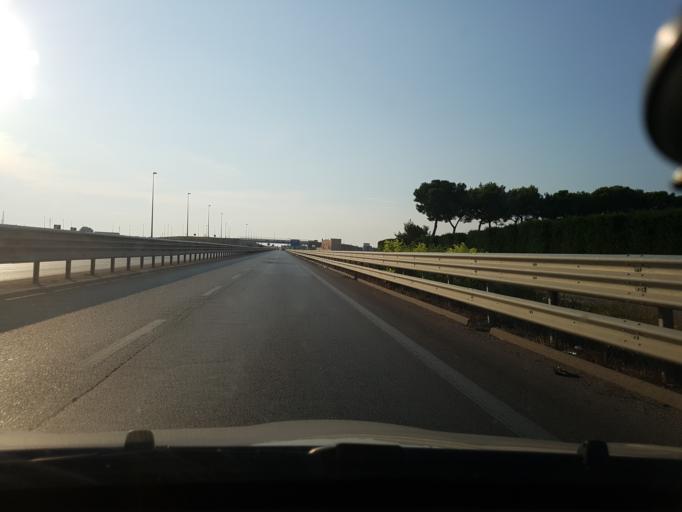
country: IT
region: Apulia
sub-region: Provincia di Foggia
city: Stornara
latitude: 41.2964
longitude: 15.8255
